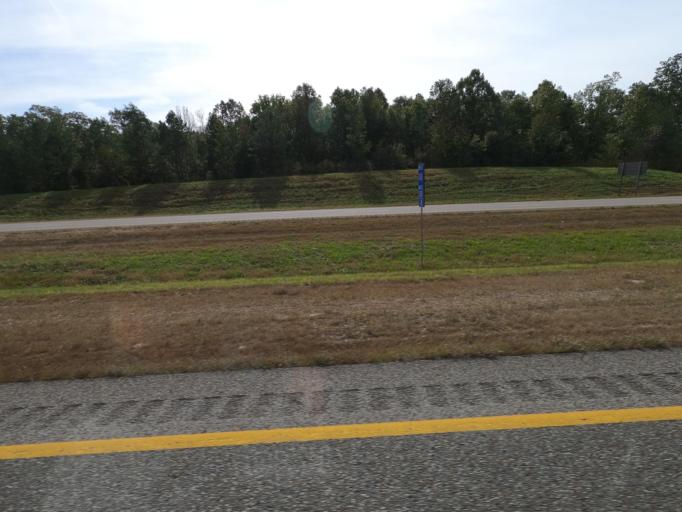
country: US
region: Tennessee
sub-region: Humphreys County
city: New Johnsonville
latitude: 35.8707
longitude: -88.0276
